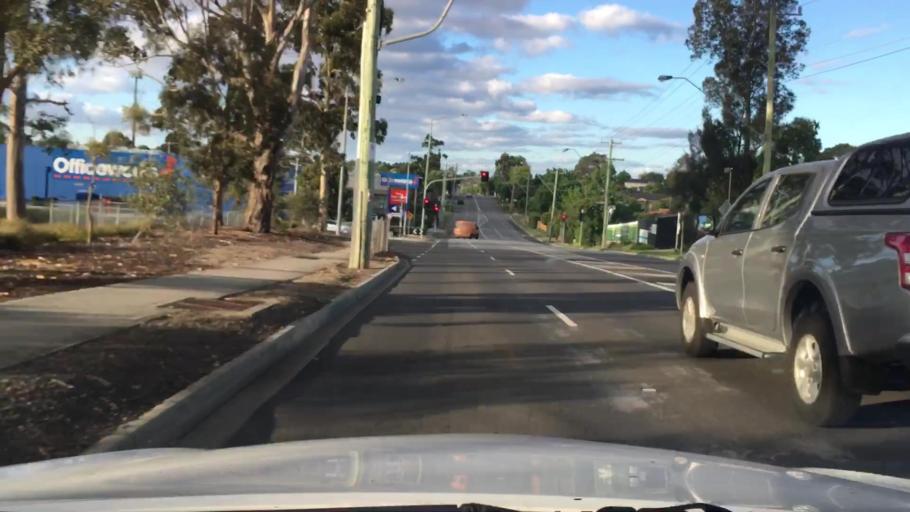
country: AU
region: Victoria
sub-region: Whitehorse
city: Box Hill South
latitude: -37.8369
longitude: 145.1351
